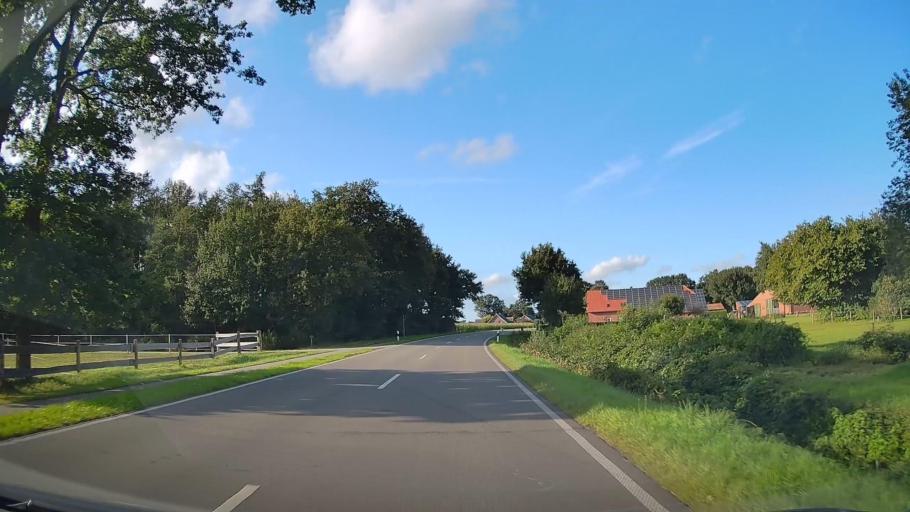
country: DE
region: Lower Saxony
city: Barssel
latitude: 53.0897
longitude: 7.7137
